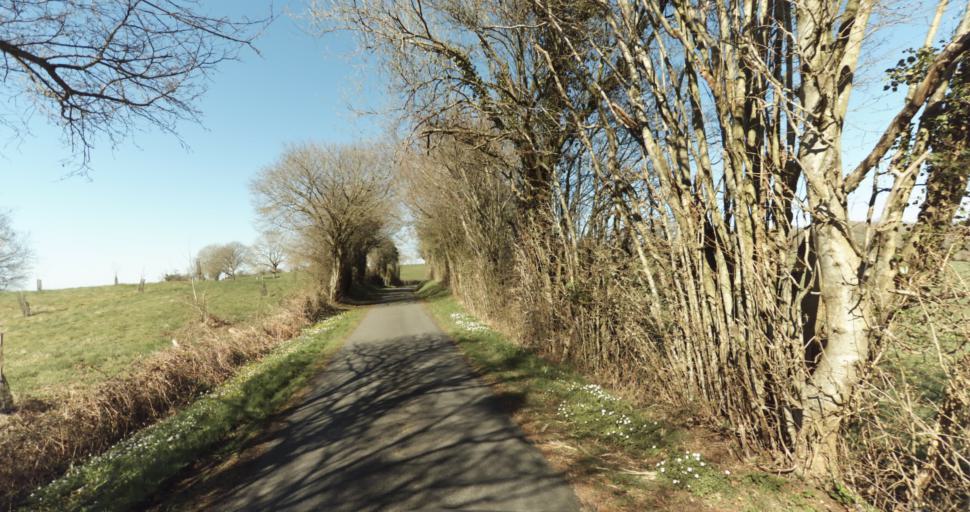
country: FR
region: Lower Normandy
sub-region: Departement de l'Orne
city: Trun
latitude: 48.9303
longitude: 0.0620
